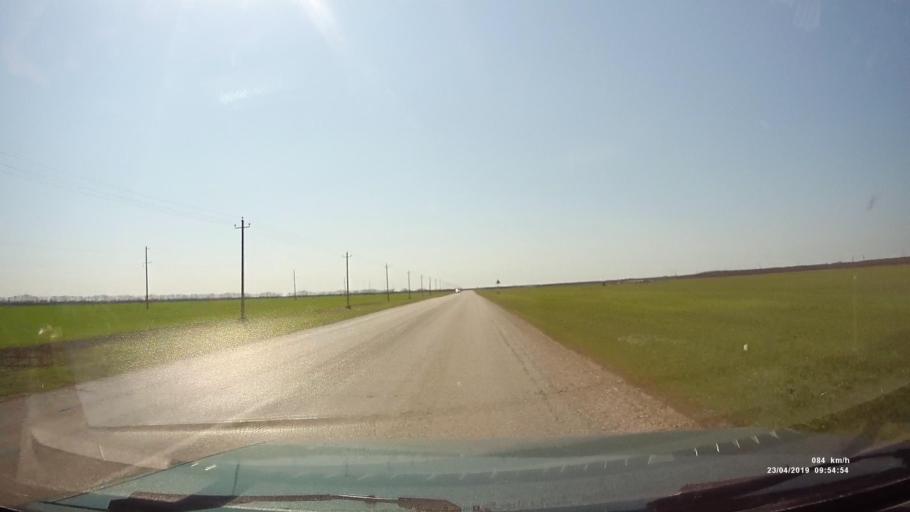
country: RU
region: Rostov
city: Orlovskiy
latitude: 46.8155
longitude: 42.0587
